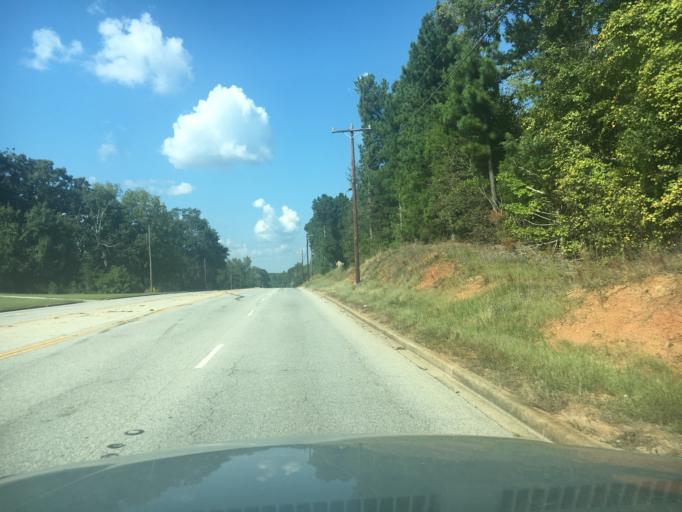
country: US
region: South Carolina
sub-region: Greenwood County
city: Ware Shoals
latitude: 34.3493
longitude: -82.2196
